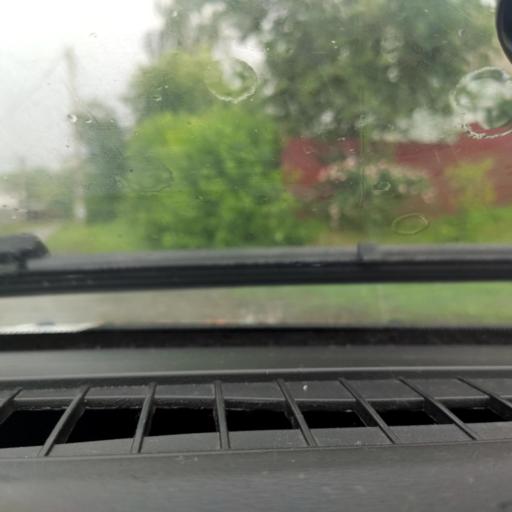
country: RU
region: Voronezj
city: Volya
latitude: 51.7536
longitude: 39.5020
